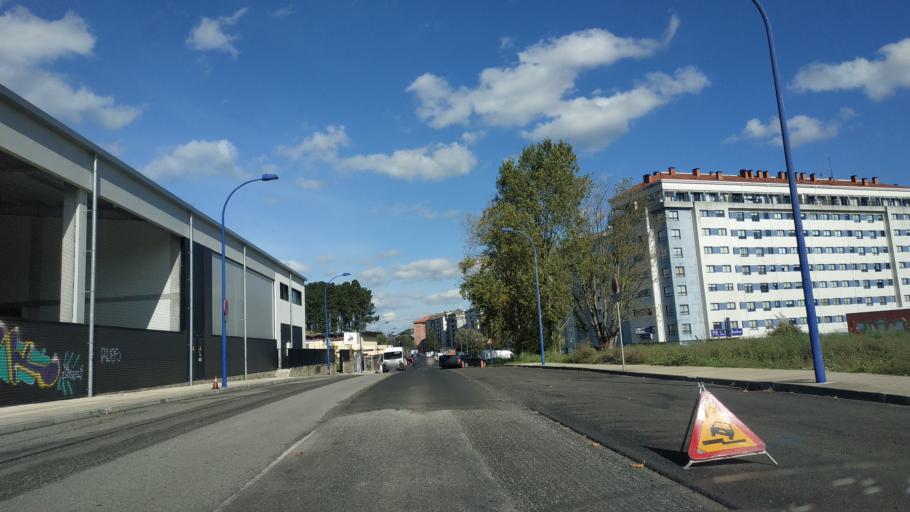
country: ES
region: Galicia
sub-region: Provincia da Coruna
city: Culleredo
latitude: 43.3145
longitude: -8.3751
